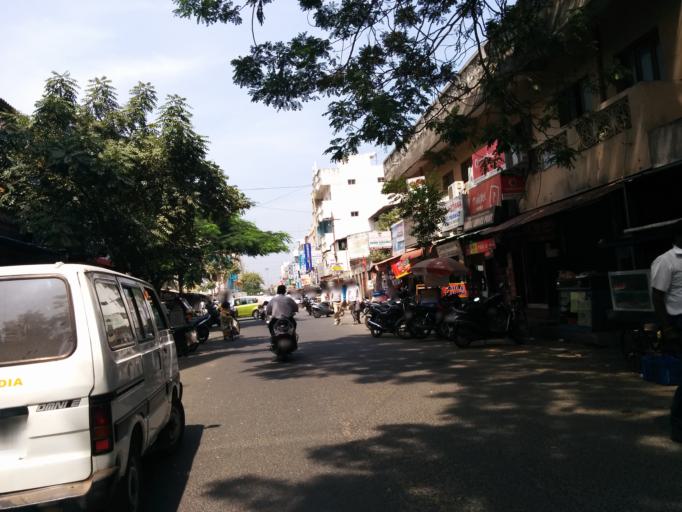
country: IN
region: Pondicherry
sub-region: Puducherry
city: Puducherry
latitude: 11.9392
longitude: 79.8298
